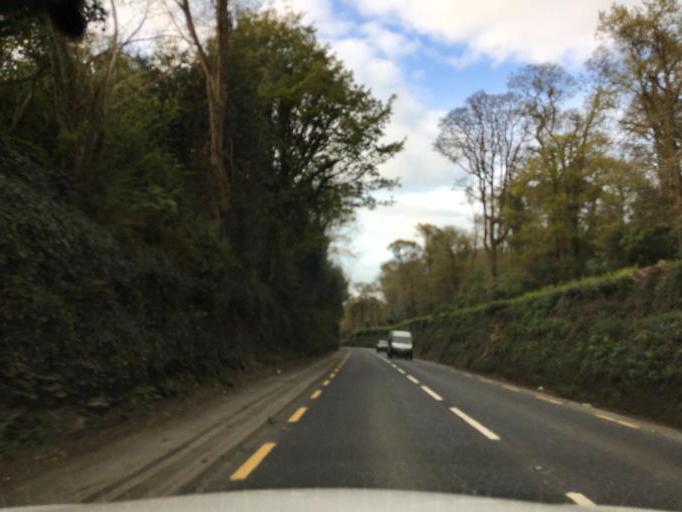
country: IE
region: Leinster
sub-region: Loch Garman
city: New Ross
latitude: 52.4156
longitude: -6.9368
